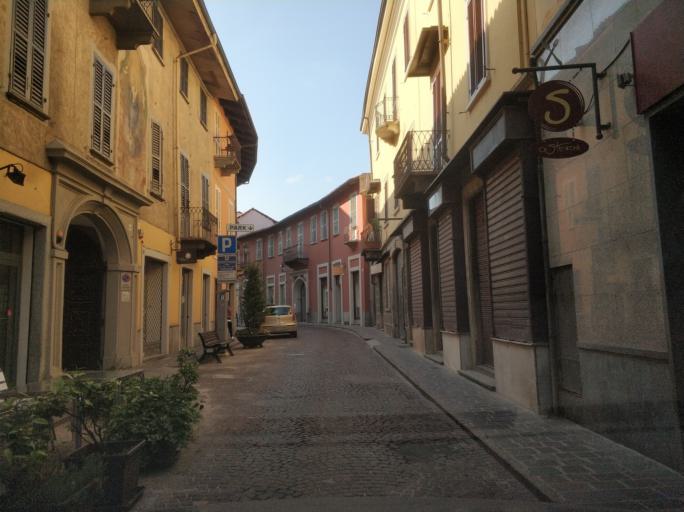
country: IT
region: Piedmont
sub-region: Provincia di Cuneo
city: Bra
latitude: 44.6976
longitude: 7.8530
